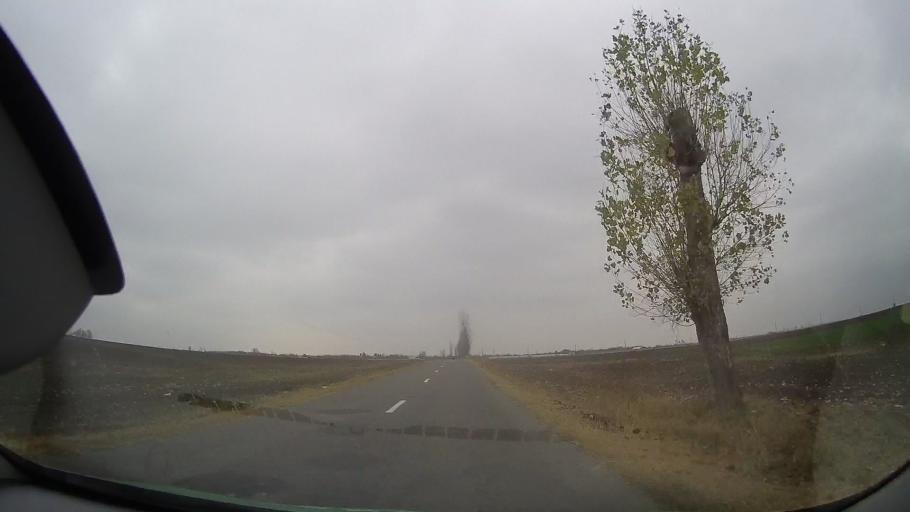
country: RO
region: Ialomita
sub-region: Comuna Valea Macrisului
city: Valea Macrisului
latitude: 44.7359
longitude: 26.8504
